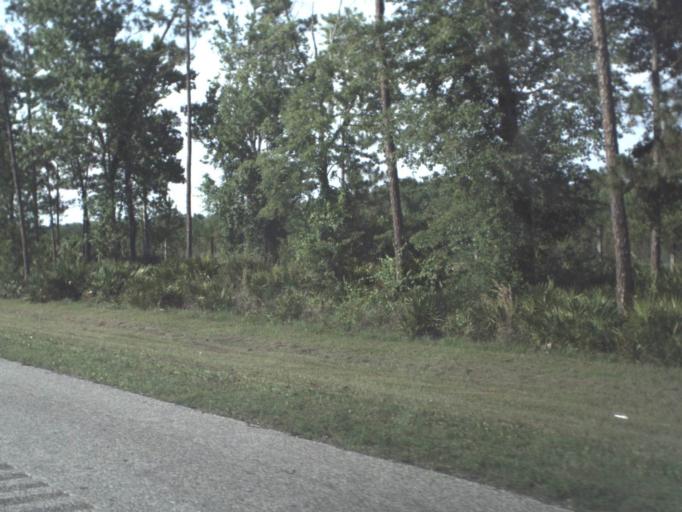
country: US
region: Florida
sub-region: Saint Johns County
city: Saint Augustine Shores
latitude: 29.7236
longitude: -81.3366
